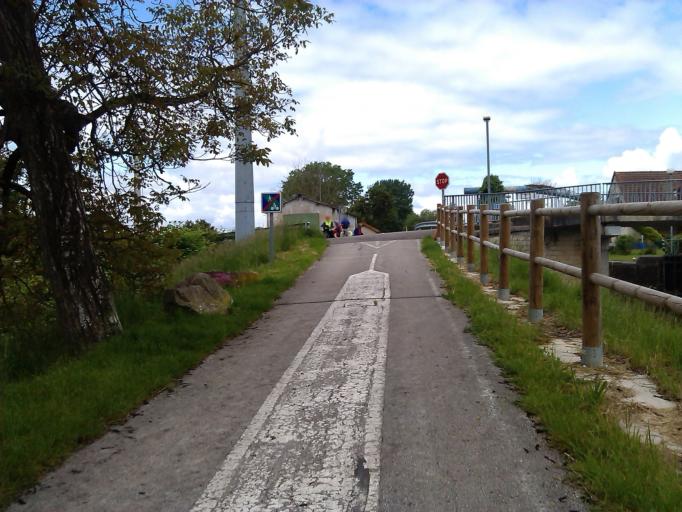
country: FR
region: Bourgogne
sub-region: Departement de Saone-et-Loire
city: Champforgeuil
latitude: 46.8336
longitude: 4.8390
